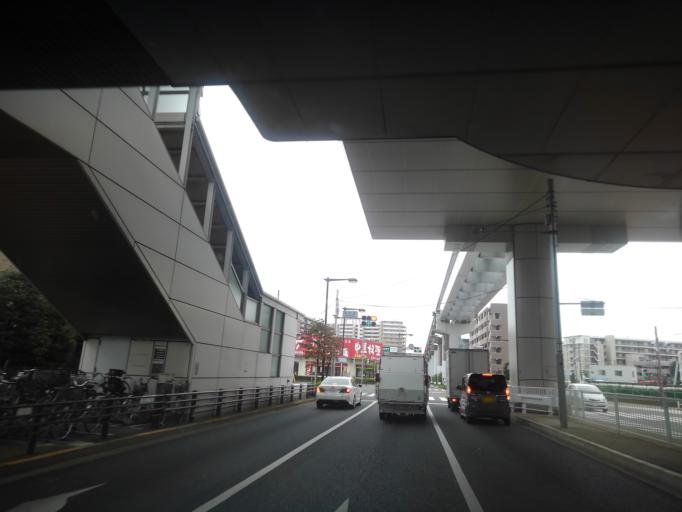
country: JP
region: Tokyo
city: Higashimurayama-shi
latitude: 35.7392
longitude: 139.4167
